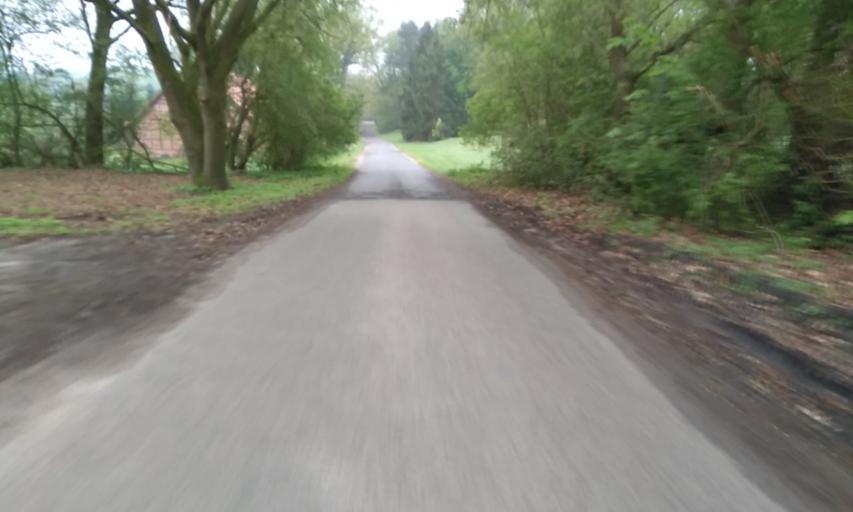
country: DE
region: Lower Saxony
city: Bliedersdorf
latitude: 53.4605
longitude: 9.5463
